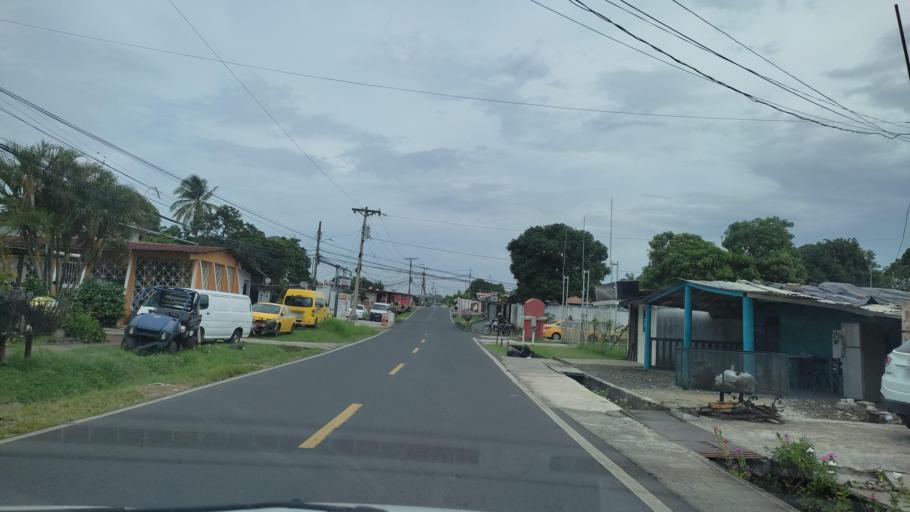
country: PA
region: Panama
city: San Miguelito
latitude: 9.0476
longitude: -79.4303
